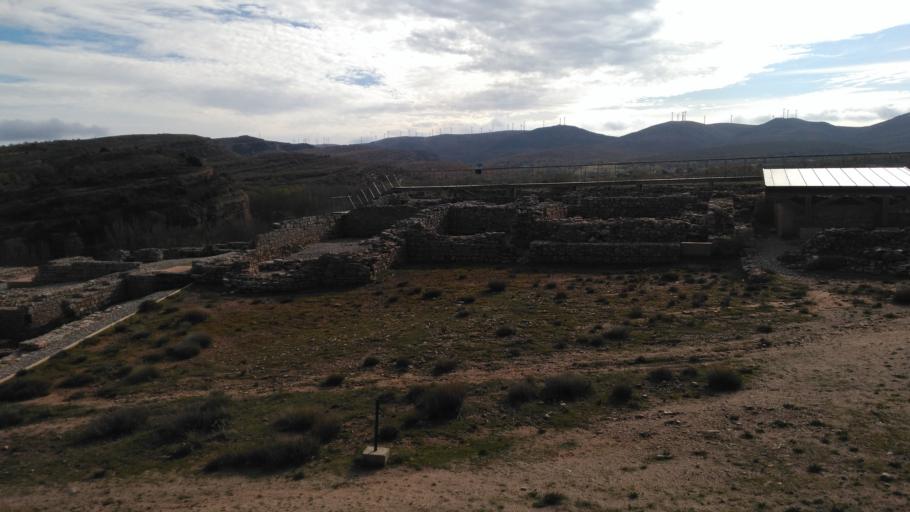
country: ES
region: Castille and Leon
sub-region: Provincia de Soria
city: Montejo de Tiermes
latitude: 41.3315
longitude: -3.1489
